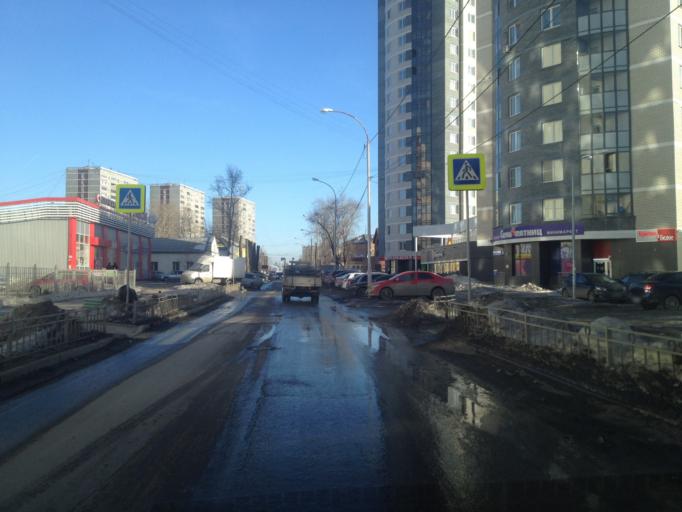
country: RU
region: Sverdlovsk
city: Yekaterinburg
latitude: 56.8725
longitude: 60.5457
